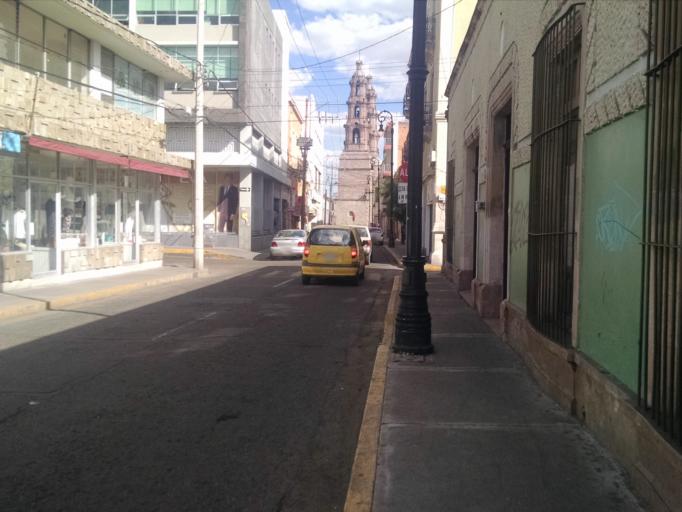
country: MX
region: Aguascalientes
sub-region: Aguascalientes
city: Aguascalientes
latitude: 21.8821
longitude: -102.2977
